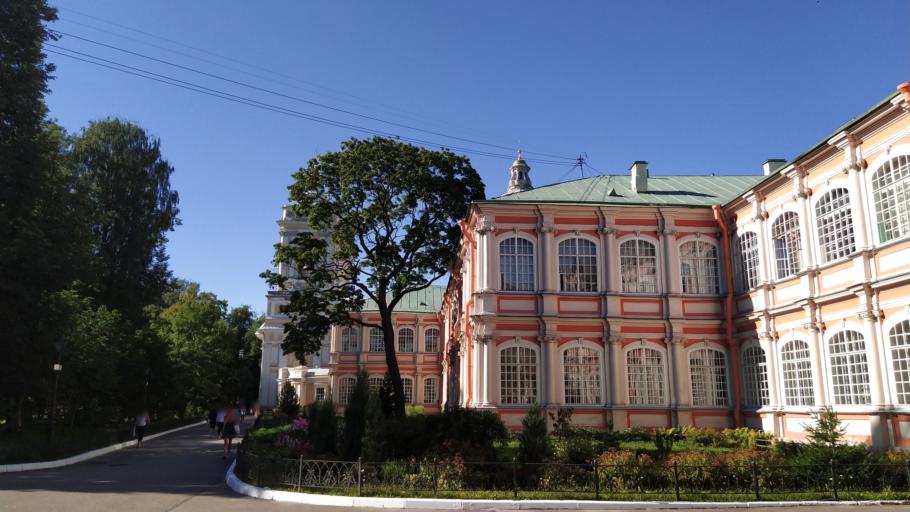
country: RU
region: St.-Petersburg
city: Centralniy
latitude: 59.9200
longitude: 30.3898
